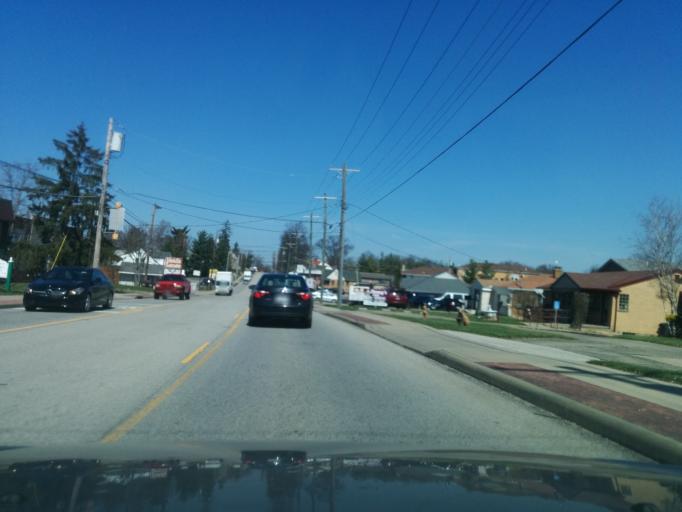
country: US
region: Ohio
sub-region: Hamilton County
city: White Oak
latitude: 39.2052
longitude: -84.5995
